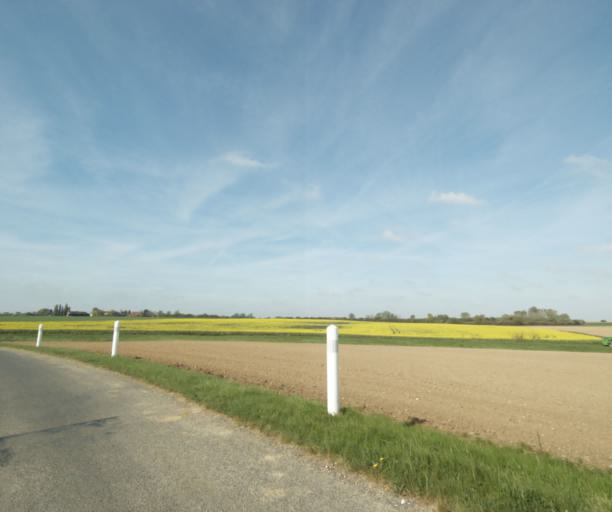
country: FR
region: Ile-de-France
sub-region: Departement de Seine-et-Marne
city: Nangis
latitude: 48.5821
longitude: 3.0465
